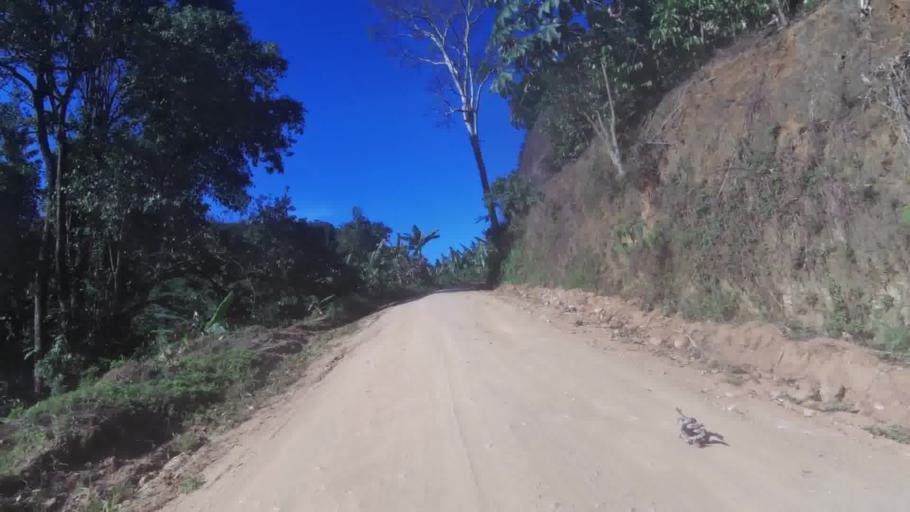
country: BR
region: Espirito Santo
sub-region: Iconha
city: Iconha
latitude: -20.7566
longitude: -40.8155
